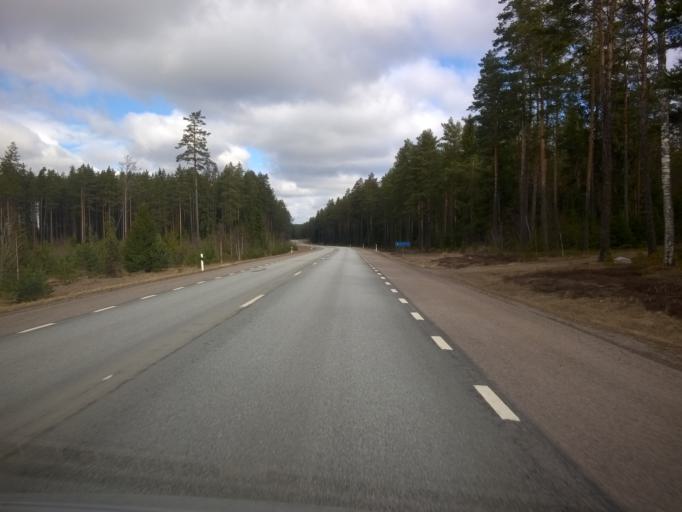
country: SE
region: Uppsala
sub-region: Tierps Kommun
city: Tierp
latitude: 60.1976
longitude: 17.4809
